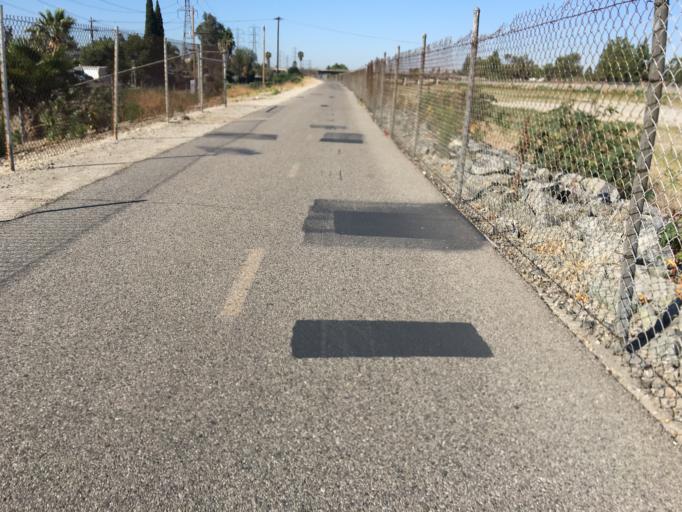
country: US
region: California
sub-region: Los Angeles County
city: West Whittier-Los Nietos
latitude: 33.9787
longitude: -118.0802
